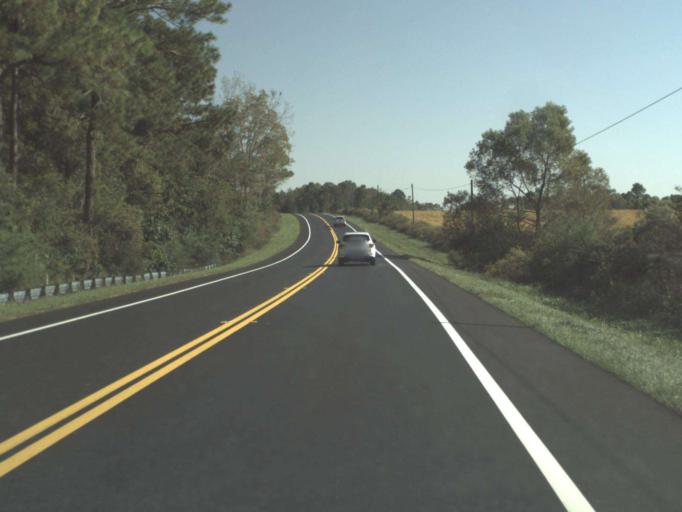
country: US
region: Alabama
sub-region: Covington County
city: Florala
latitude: 30.8887
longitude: -86.2790
